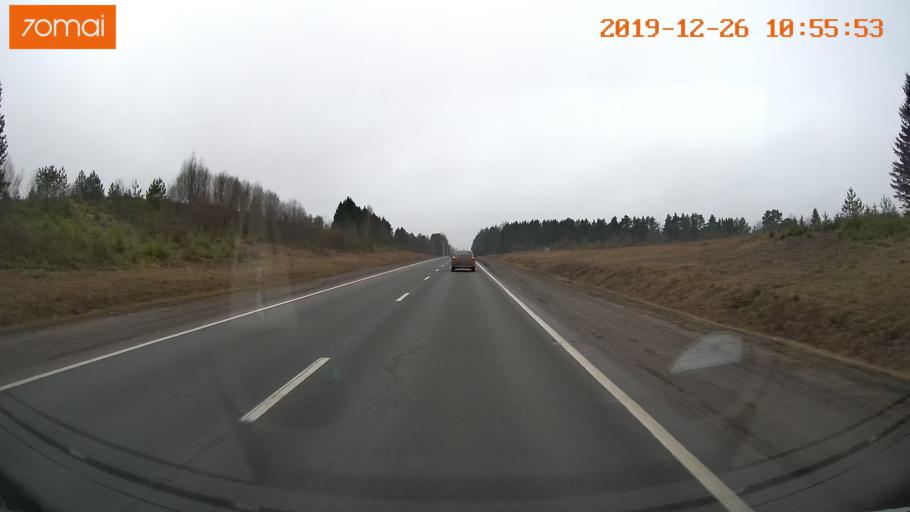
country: RU
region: Vologda
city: Molochnoye
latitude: 59.1849
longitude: 39.5703
